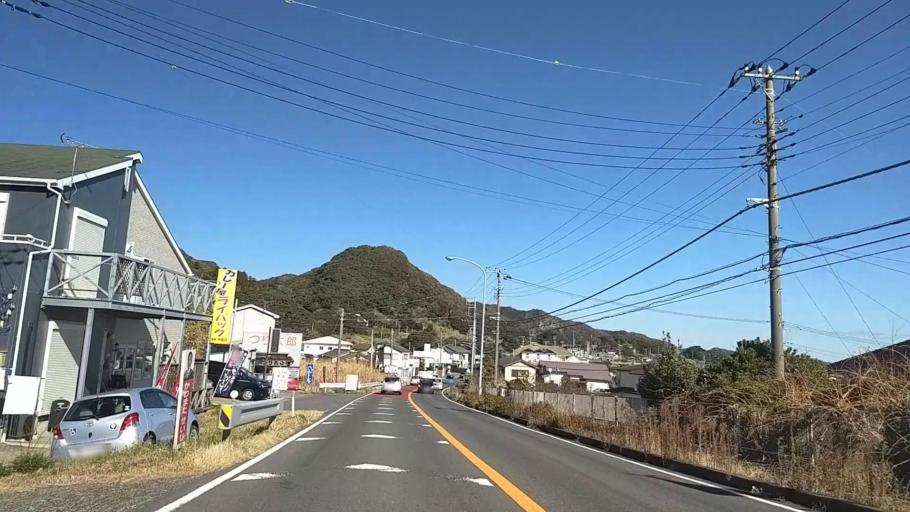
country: JP
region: Chiba
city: Kawaguchi
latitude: 35.0615
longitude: 140.0735
